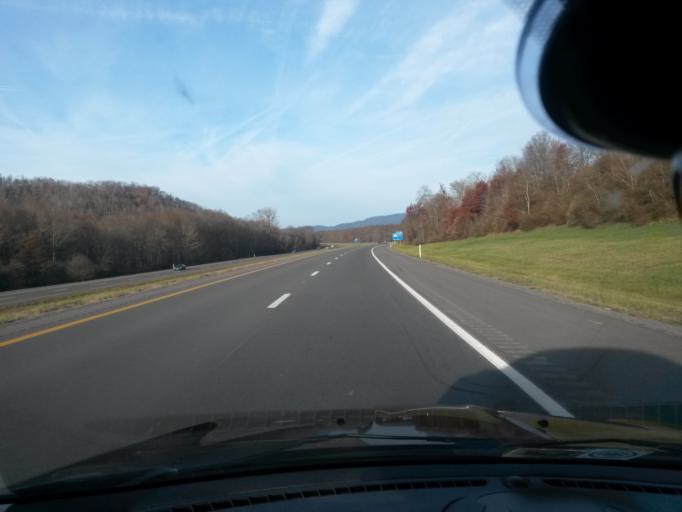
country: US
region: West Virginia
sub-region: Greenbrier County
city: Rainelle
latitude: 37.9062
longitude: -80.6062
